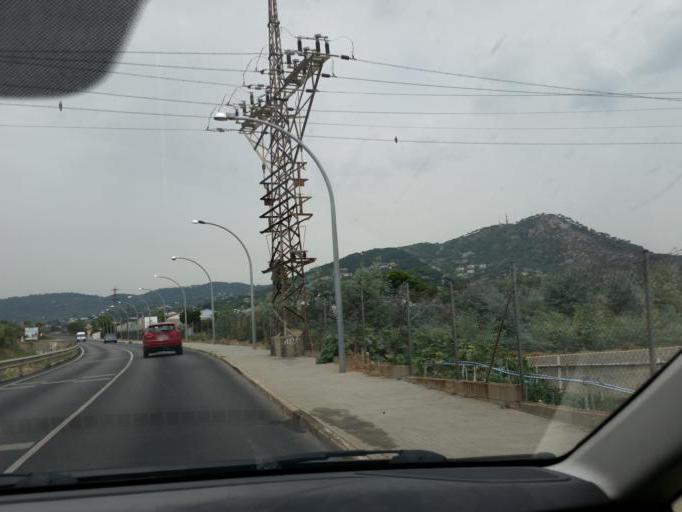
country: ES
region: Catalonia
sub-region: Provincia de Barcelona
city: Vilassar de Mar
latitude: 41.5092
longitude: 2.3842
